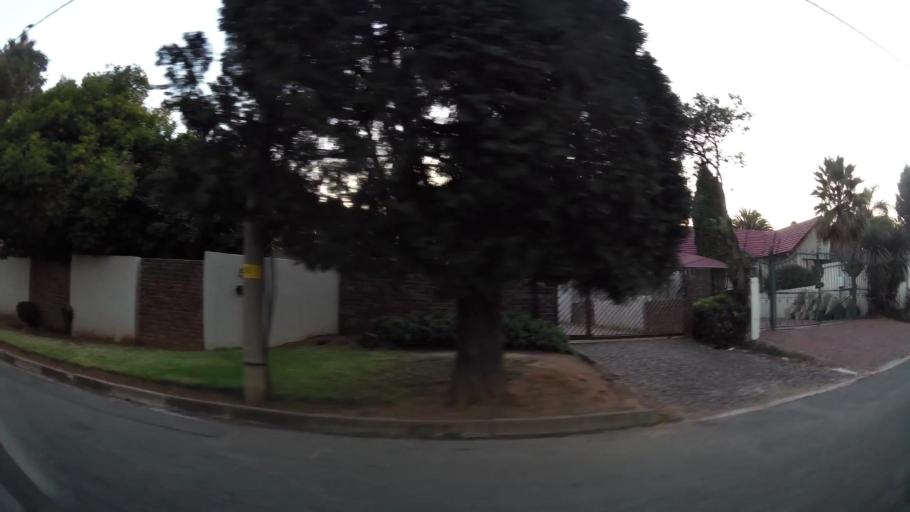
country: ZA
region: Gauteng
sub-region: Ekurhuleni Metropolitan Municipality
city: Tembisa
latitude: -26.0607
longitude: 28.2370
